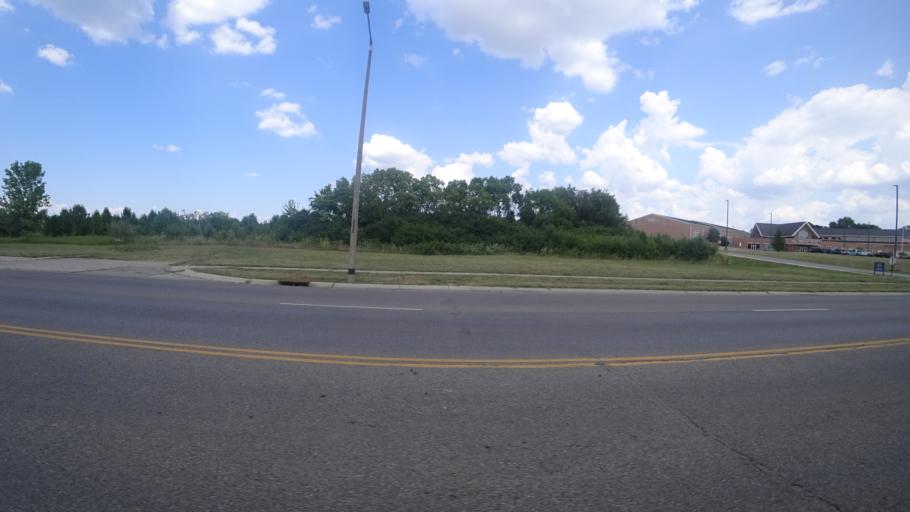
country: US
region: Ohio
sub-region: Butler County
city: New Miami
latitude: 39.4227
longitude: -84.5557
